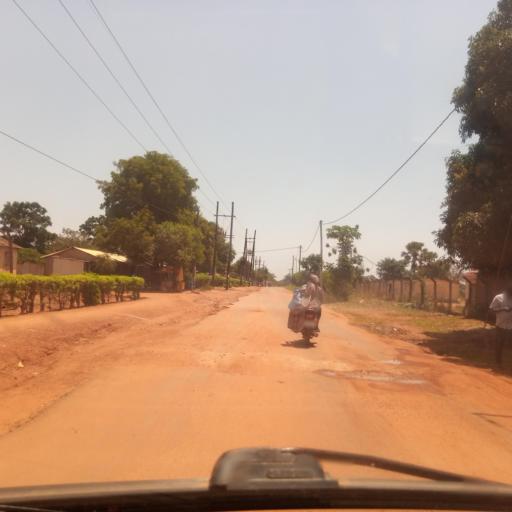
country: UG
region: Northern Region
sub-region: Lira District
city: Lira
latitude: 2.2541
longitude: 32.9000
